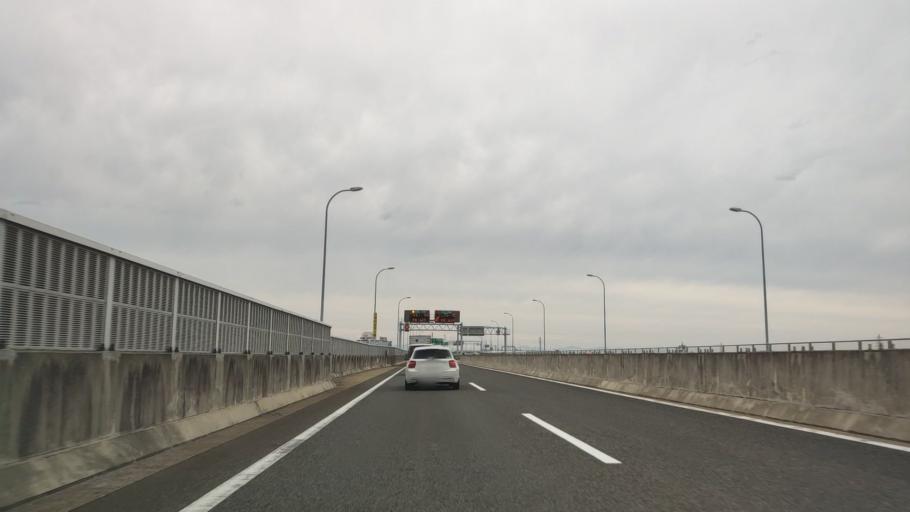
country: JP
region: Aichi
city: Iwakura
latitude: 35.2666
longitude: 136.8365
